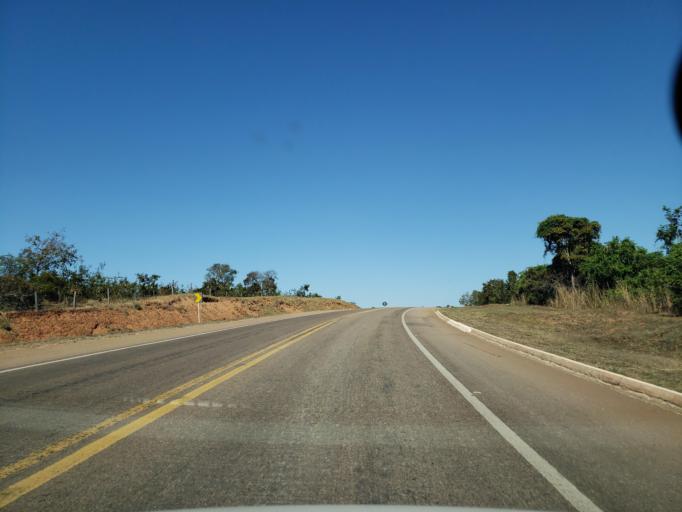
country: BR
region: Mato Grosso
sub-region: Poxoreo
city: Poxoreo
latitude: -15.7794
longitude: -54.3676
